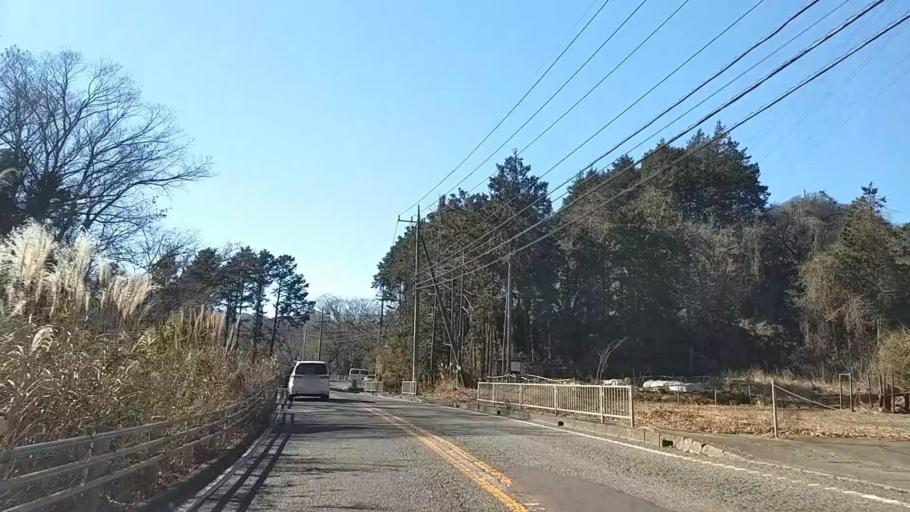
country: JP
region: Yamanashi
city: Uenohara
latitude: 35.6177
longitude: 139.0939
